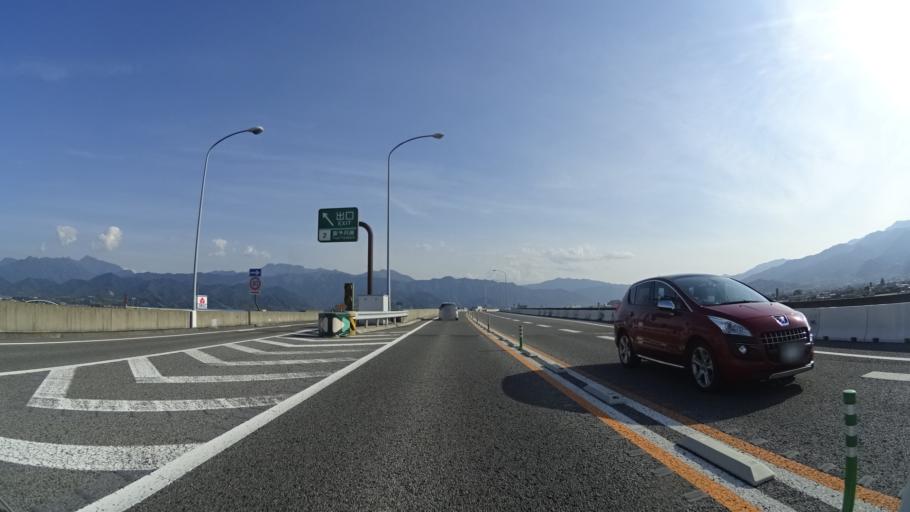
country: JP
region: Ehime
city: Saijo
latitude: 33.9205
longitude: 133.0744
